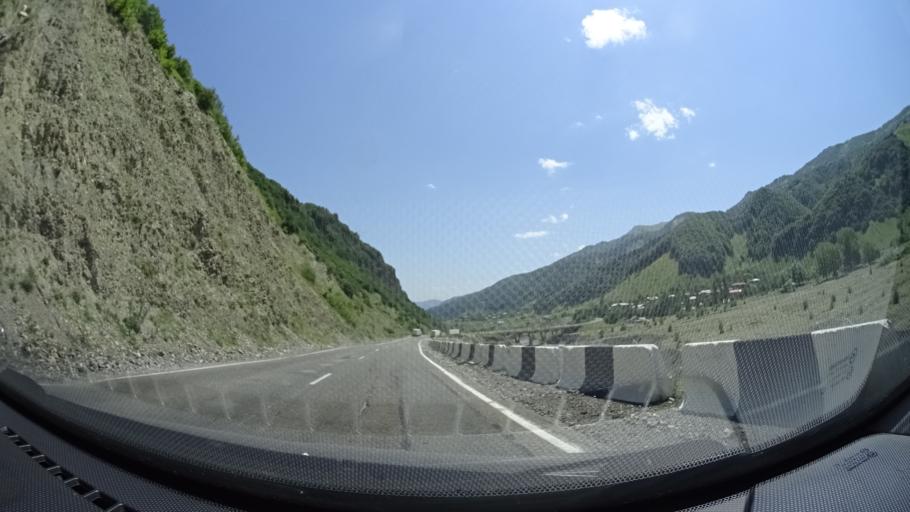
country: GE
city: Gudauri
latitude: 42.4322
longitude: 44.5044
